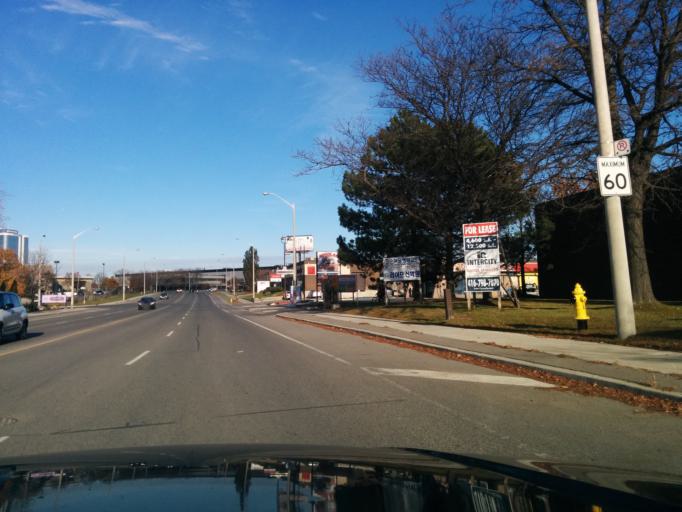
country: CA
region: Ontario
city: Etobicoke
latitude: 43.6191
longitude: -79.5633
